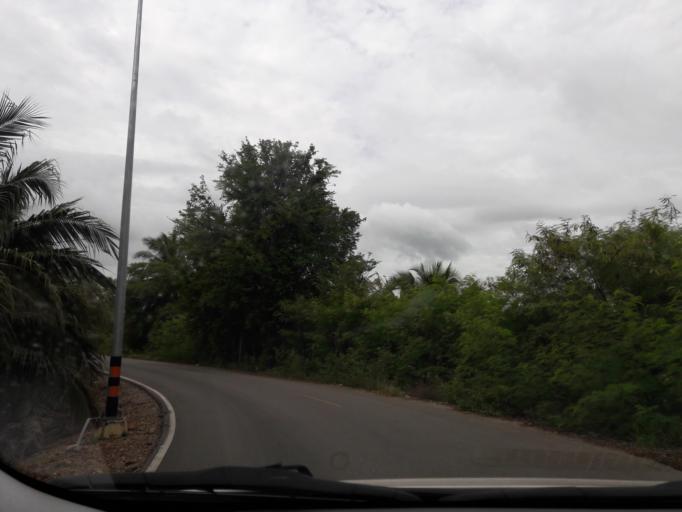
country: TH
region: Ratchaburi
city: Damnoen Saduak
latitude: 13.5405
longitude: 99.9574
